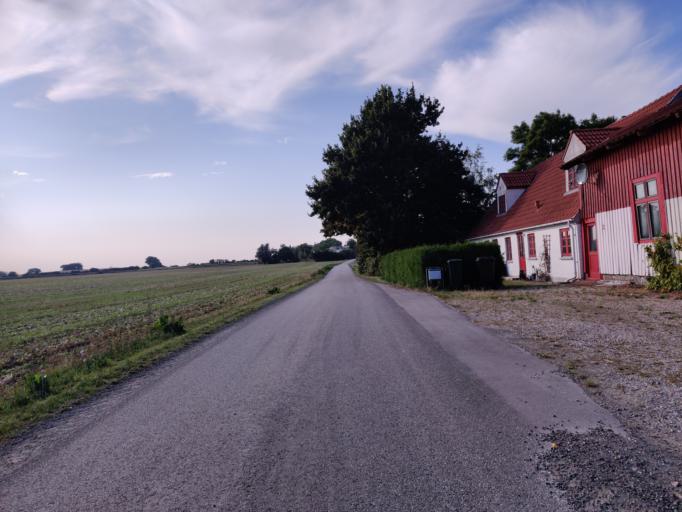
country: DK
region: Zealand
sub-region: Guldborgsund Kommune
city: Nykobing Falster
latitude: 54.6966
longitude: 11.9108
